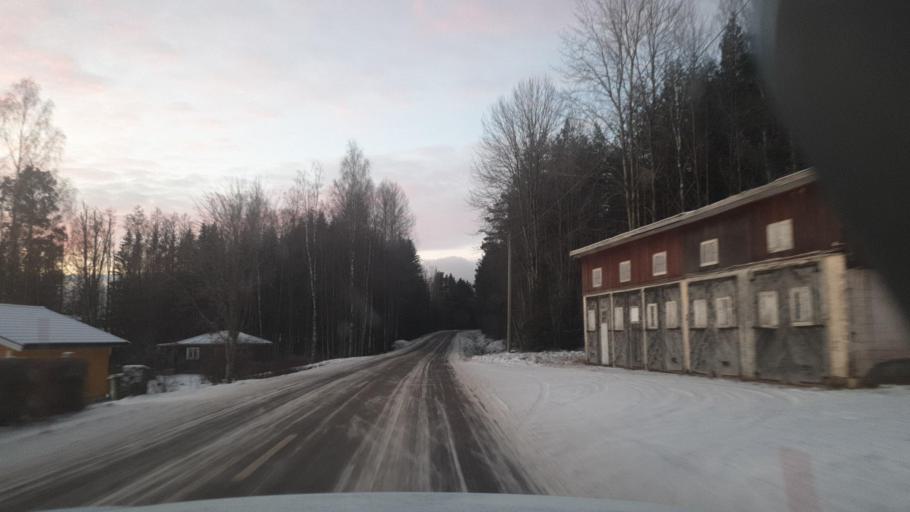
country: SE
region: Vaermland
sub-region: Grums Kommun
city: Slottsbron
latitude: 59.4513
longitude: 12.8837
